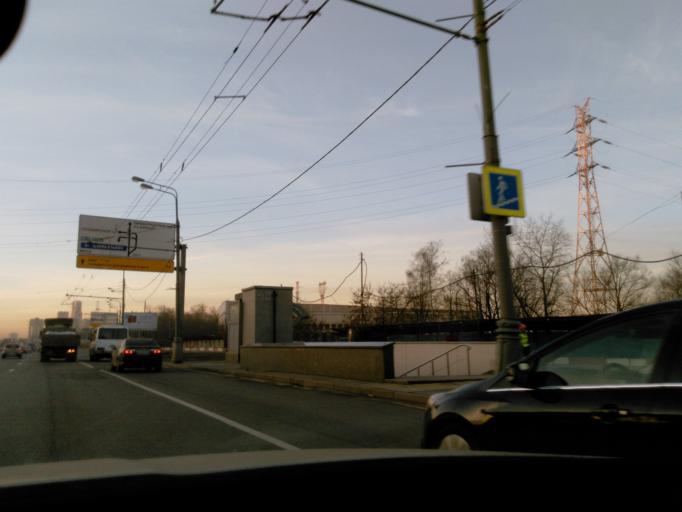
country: RU
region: Moskovskaya
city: Levoberezhnyy
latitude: 55.8438
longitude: 37.4780
